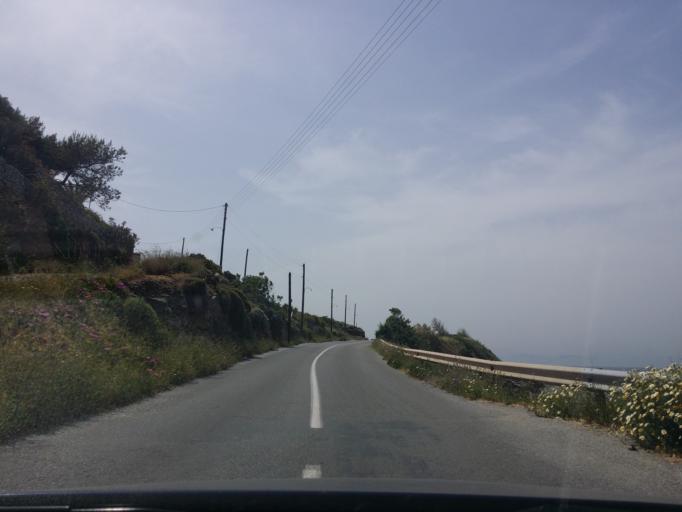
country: GR
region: South Aegean
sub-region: Nomos Kykladon
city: Kea
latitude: 37.6619
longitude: 24.3208
